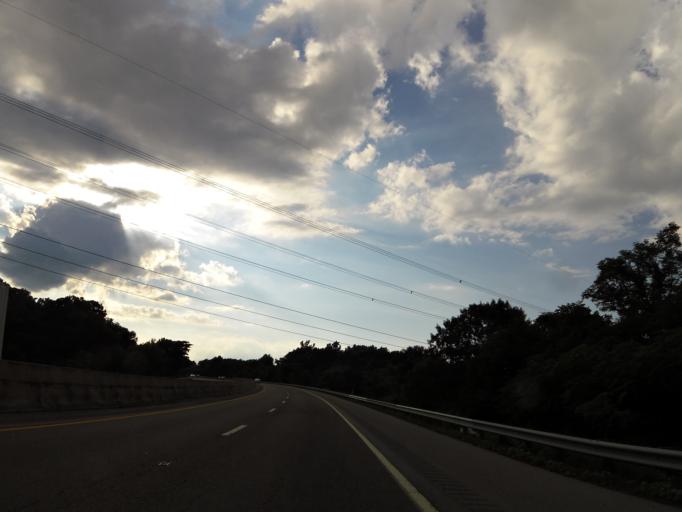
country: US
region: Tennessee
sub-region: Blount County
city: Louisville
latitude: 35.8650
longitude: -84.0350
